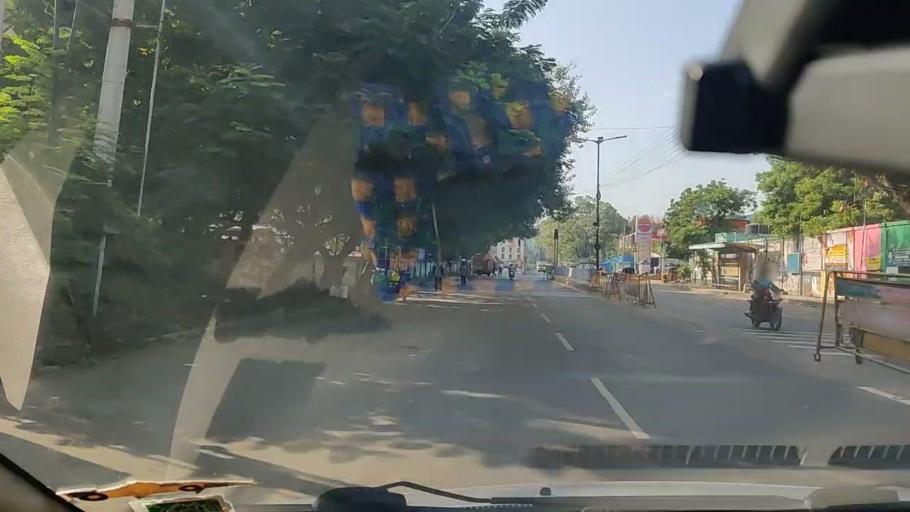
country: IN
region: Tamil Nadu
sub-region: Chennai
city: George Town
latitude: 13.1028
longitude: 80.2740
